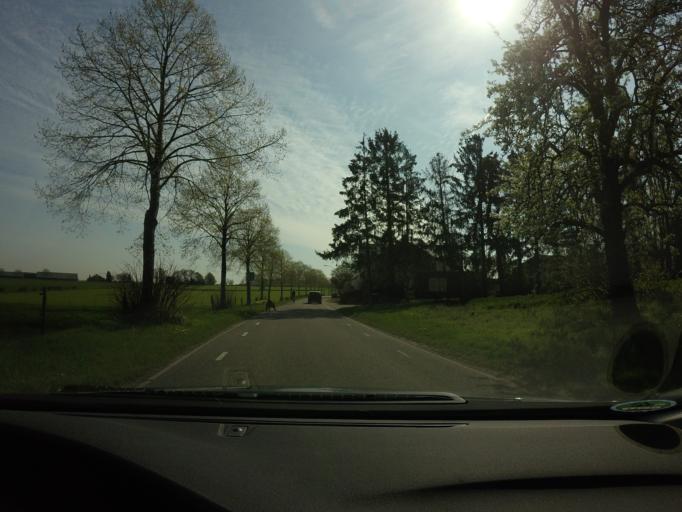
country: NL
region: Limburg
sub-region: Valkenburg aan de Geul
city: Berg
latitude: 50.8428
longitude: 5.7917
